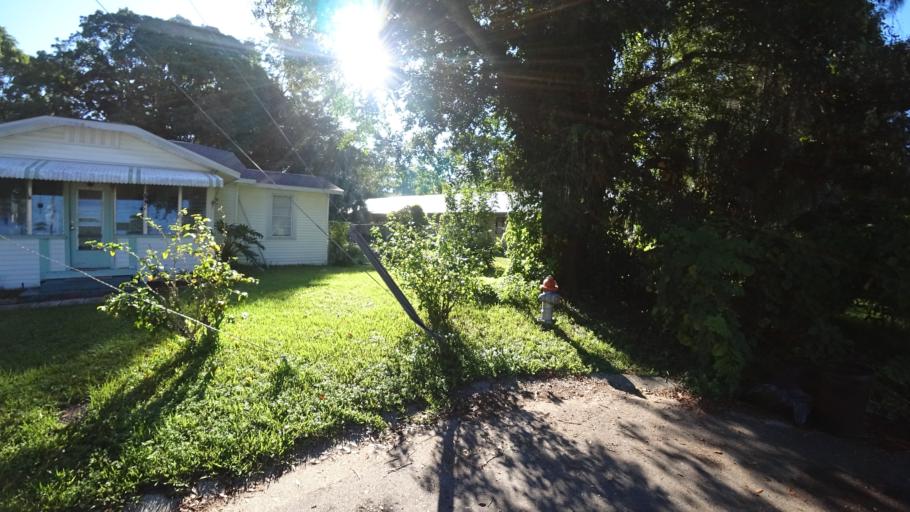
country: US
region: Florida
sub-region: Manatee County
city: South Bradenton
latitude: 27.4781
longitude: -82.5736
